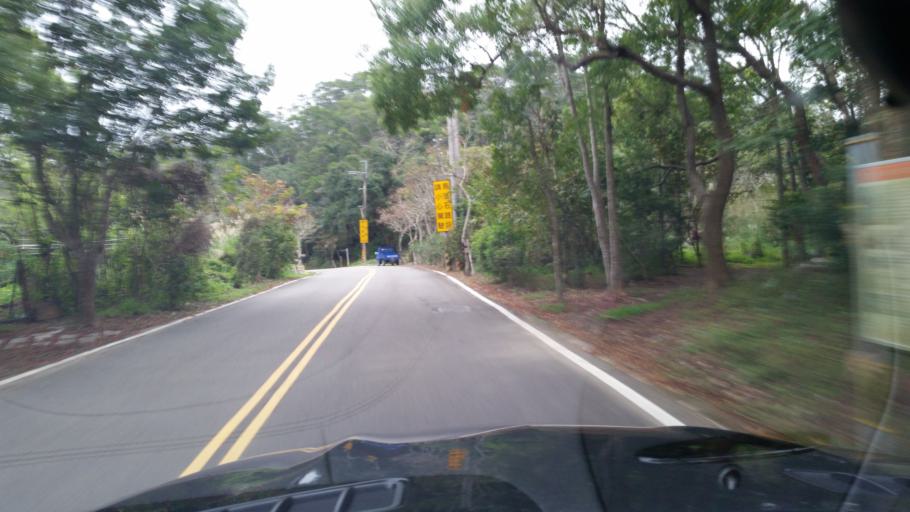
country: TW
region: Taiwan
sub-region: Miaoli
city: Miaoli
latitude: 24.5814
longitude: 120.8823
